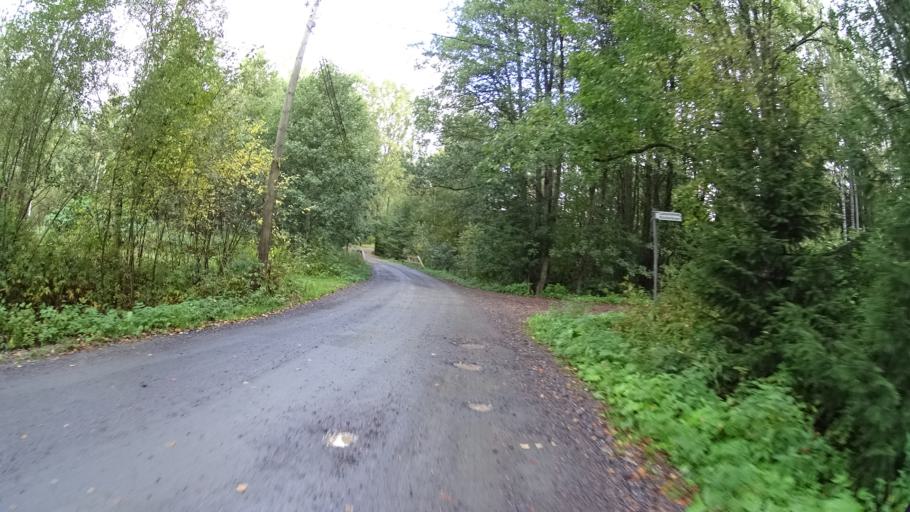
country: FI
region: Uusimaa
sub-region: Helsinki
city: Espoo
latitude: 60.2356
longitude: 24.6527
